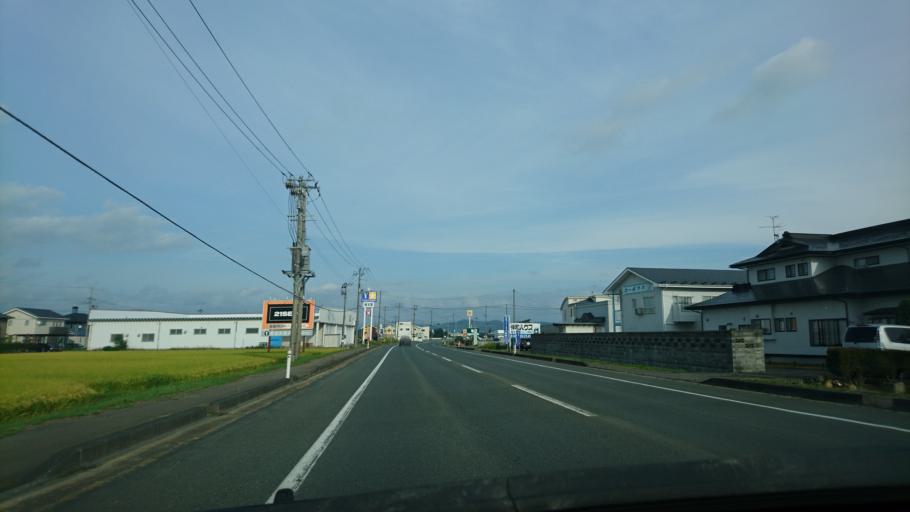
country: JP
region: Iwate
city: Kitakami
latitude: 39.3008
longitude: 141.0762
